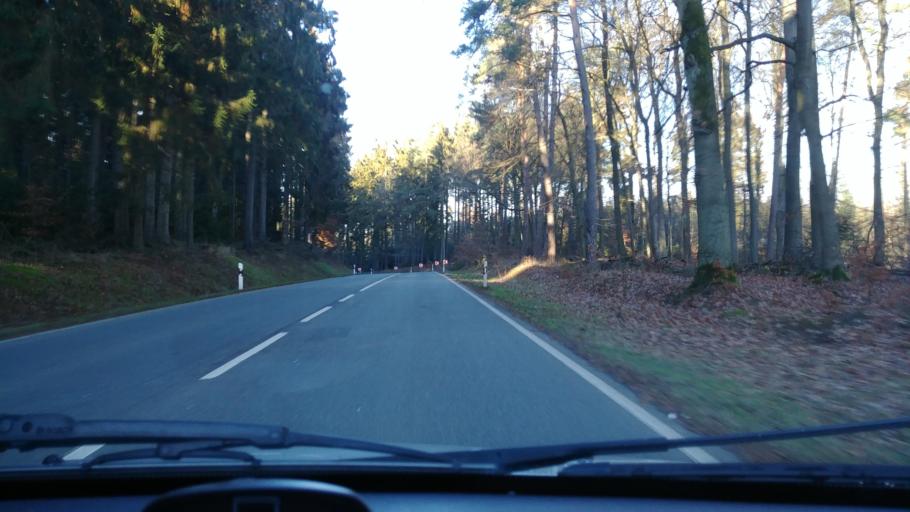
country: DE
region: Rheinland-Pfalz
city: Obertiefenbach
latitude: 50.2323
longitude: 7.8883
